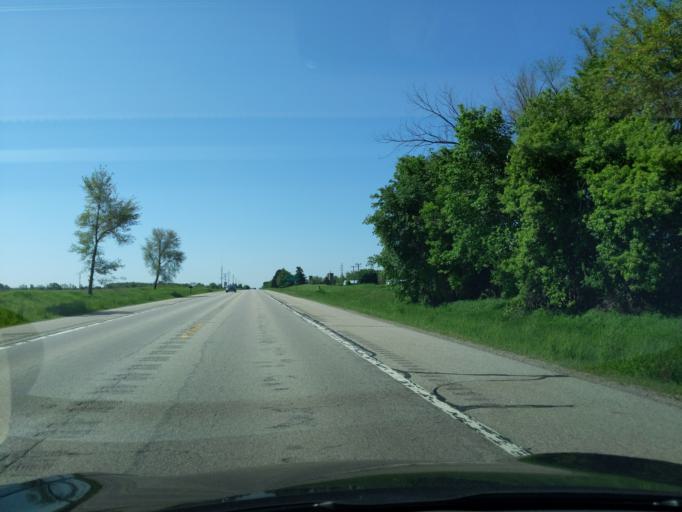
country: US
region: Michigan
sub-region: Ingham County
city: Webberville
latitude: 42.5727
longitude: -84.1923
